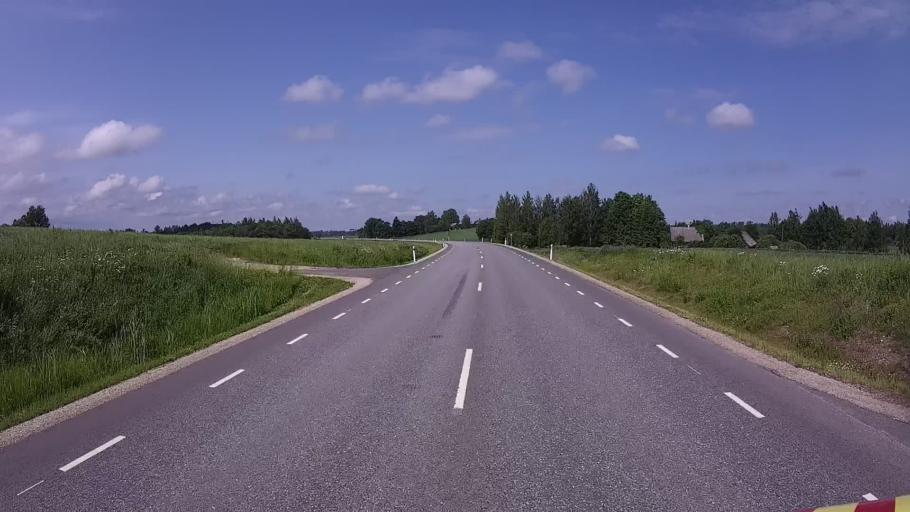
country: EE
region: Polvamaa
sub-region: Polva linn
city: Polva
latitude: 58.1778
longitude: 26.8932
